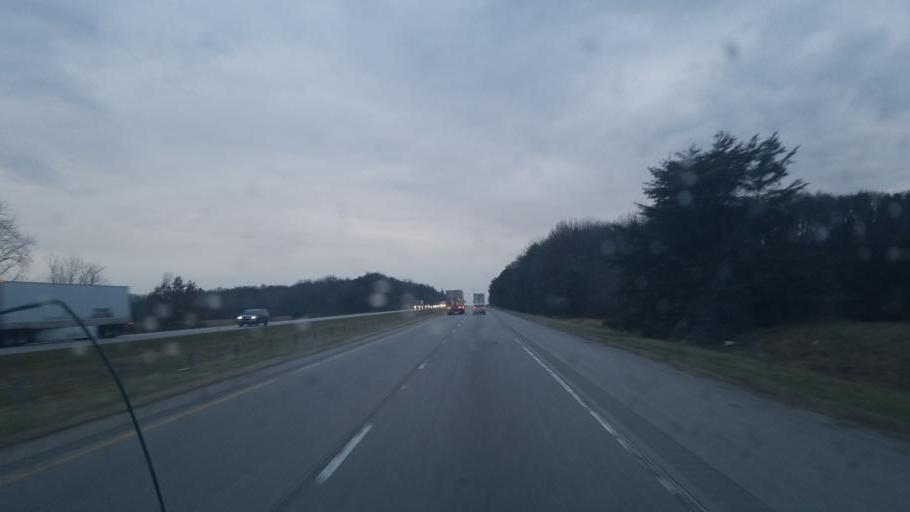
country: US
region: Indiana
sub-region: Clay County
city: Brazil
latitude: 39.4506
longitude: -87.1661
